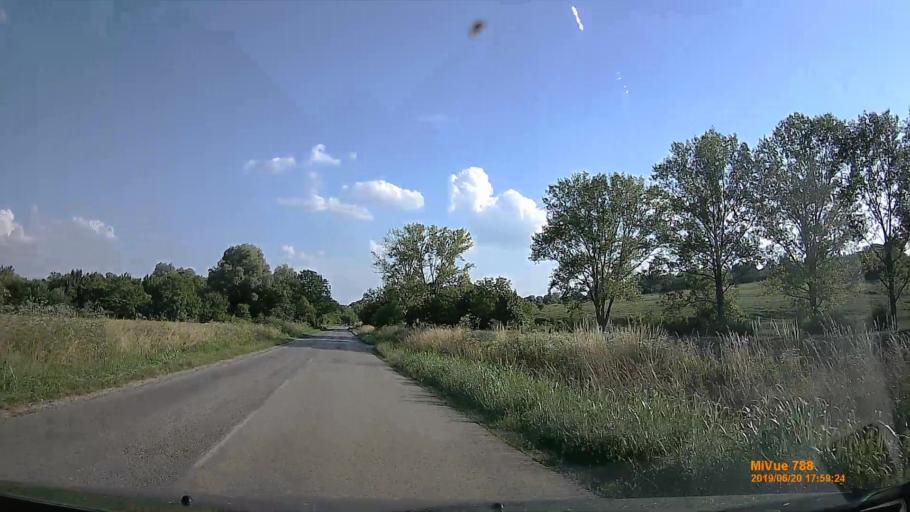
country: HU
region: Baranya
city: Buekkoesd
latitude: 46.0975
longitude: 17.9862
